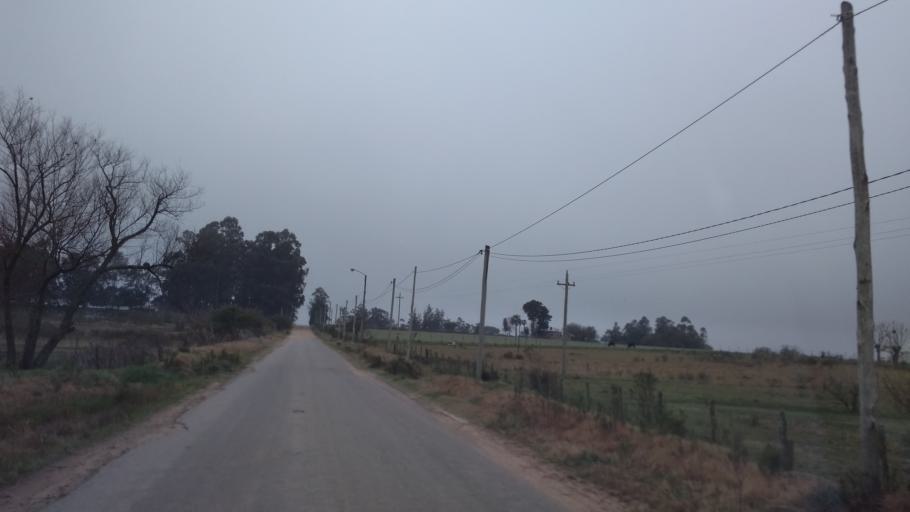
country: UY
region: Florida
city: Florida
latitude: -34.0818
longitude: -56.2039
